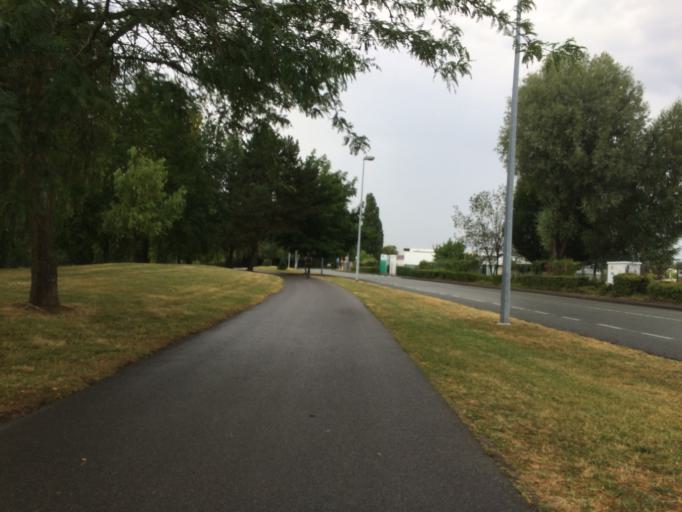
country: FR
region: Picardie
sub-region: Departement de l'Oise
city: Jaux
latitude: 49.3940
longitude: 2.7838
